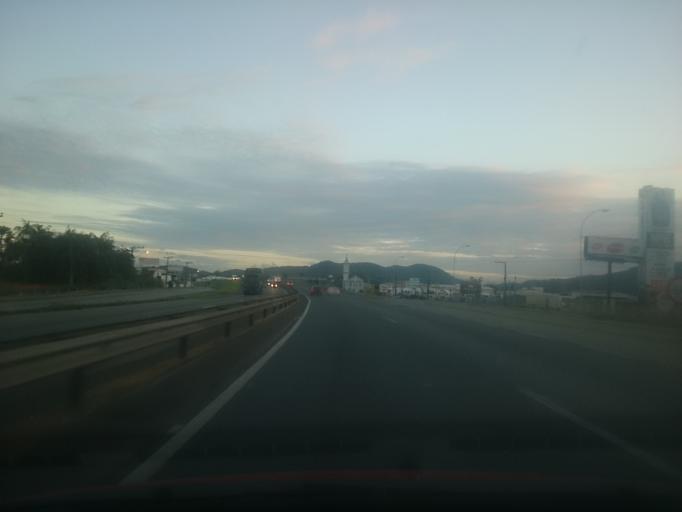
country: BR
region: Santa Catarina
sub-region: Itajai
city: Itajai
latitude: -26.8670
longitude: -48.7302
